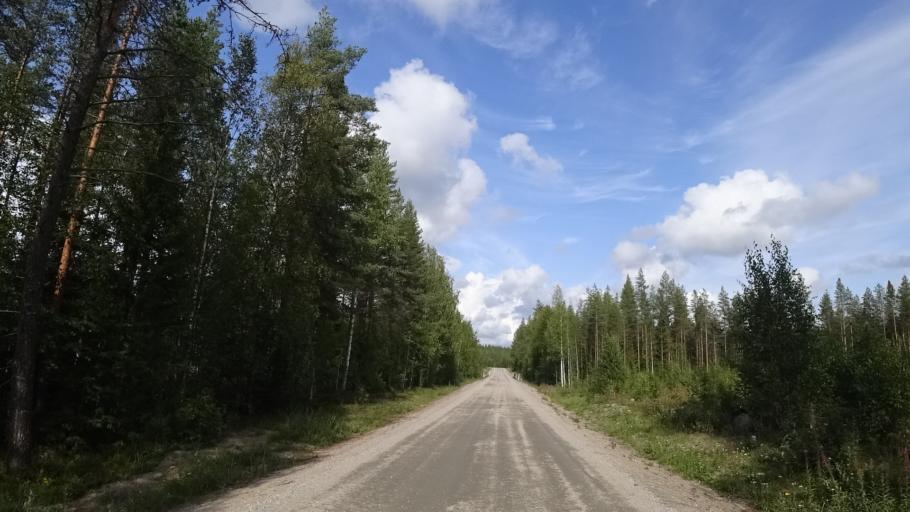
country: FI
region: North Karelia
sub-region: Pielisen Karjala
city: Lieksa
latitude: 63.5746
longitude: 30.1194
